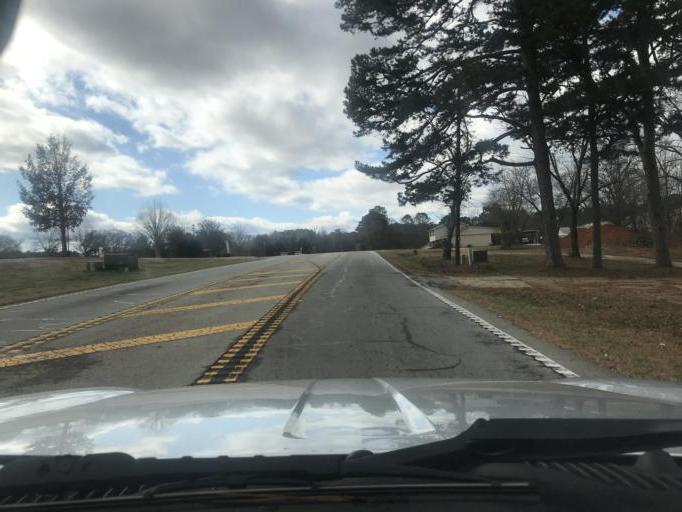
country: US
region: Georgia
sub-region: Barrow County
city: Winder
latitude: 34.0168
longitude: -83.6907
